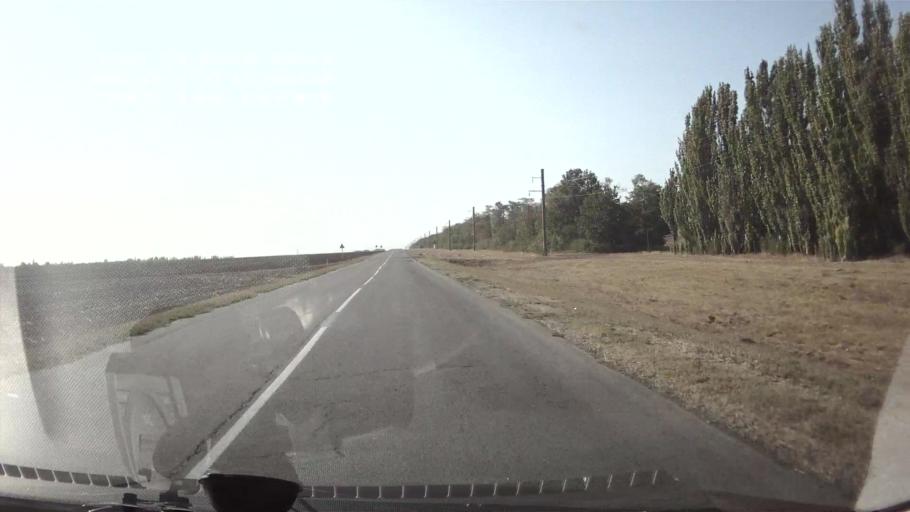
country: RU
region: Rostov
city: Tselina
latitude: 46.5196
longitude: 40.8996
